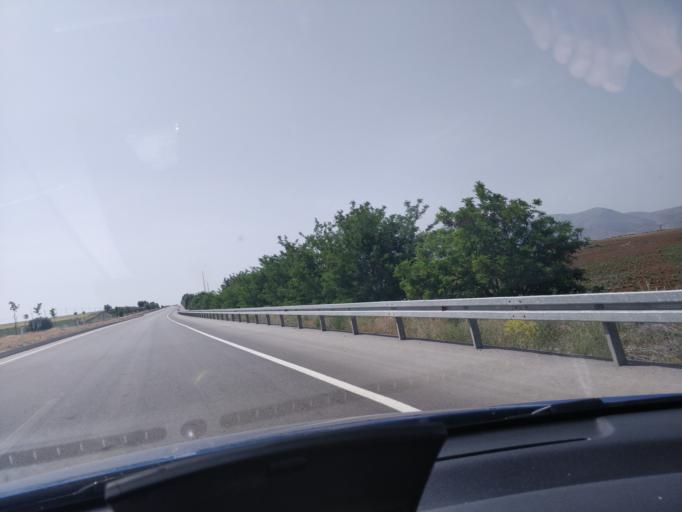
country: TR
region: Konya
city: Guneysinir
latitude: 37.3250
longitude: 32.8397
